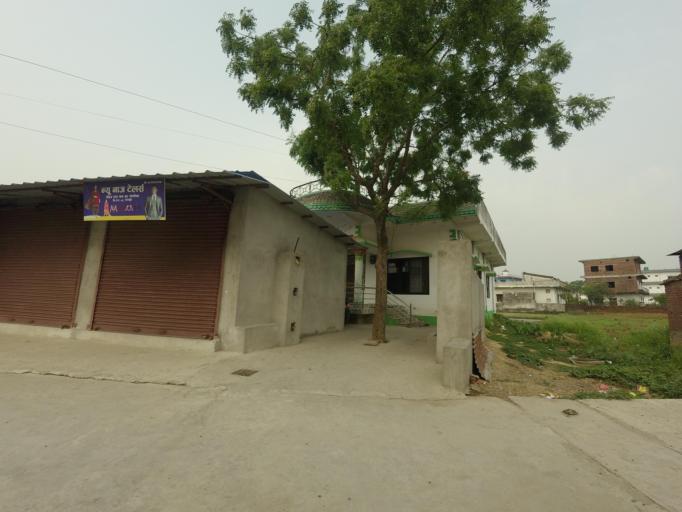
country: NP
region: Western Region
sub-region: Lumbini Zone
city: Bhairahawa
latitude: 27.4916
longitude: 83.4515
